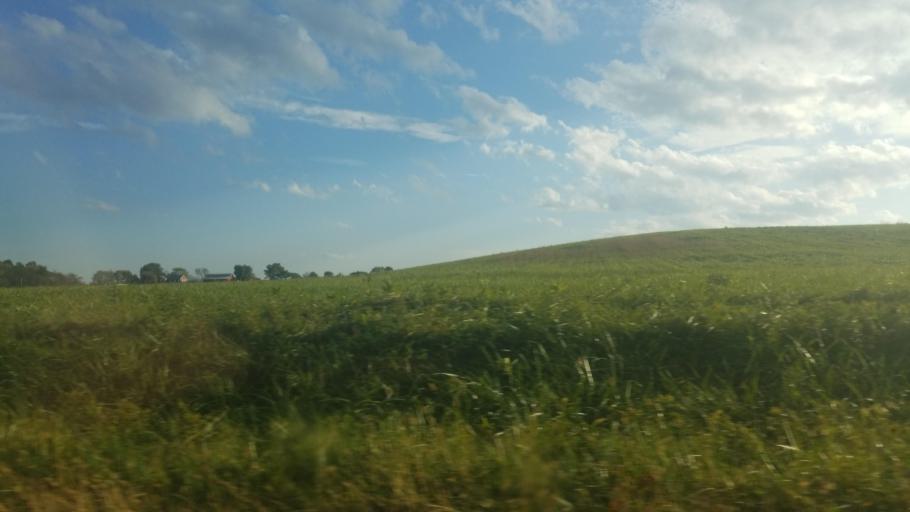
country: US
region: Illinois
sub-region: Saline County
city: Carrier Mills
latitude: 37.8049
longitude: -88.6686
